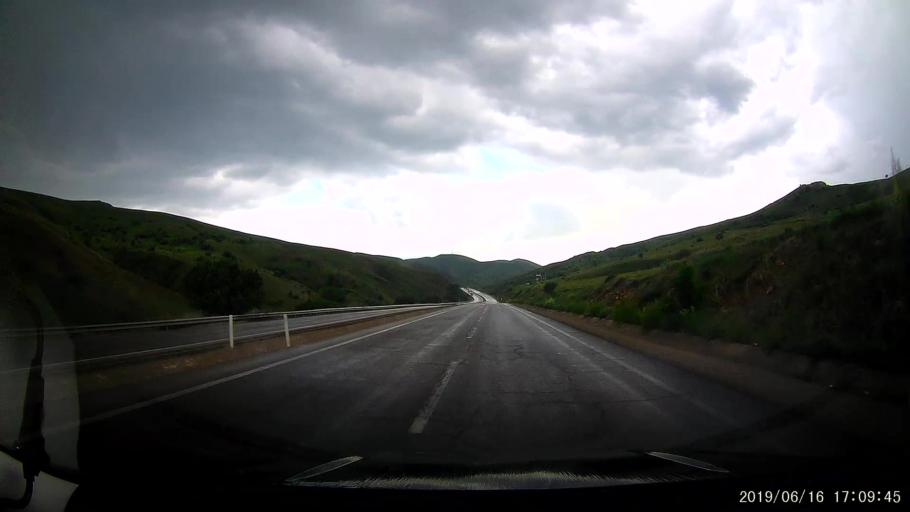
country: TR
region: Erzurum
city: Askale
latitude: 39.8899
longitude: 40.6479
